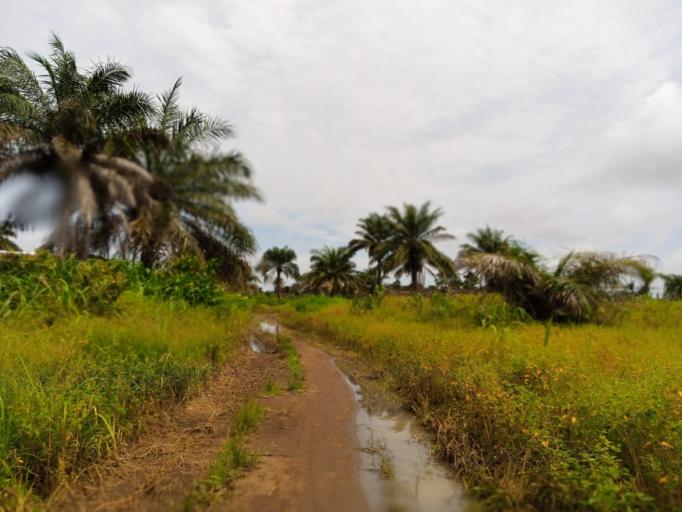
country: SL
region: Northern Province
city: Masoyila
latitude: 8.5893
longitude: -13.1942
